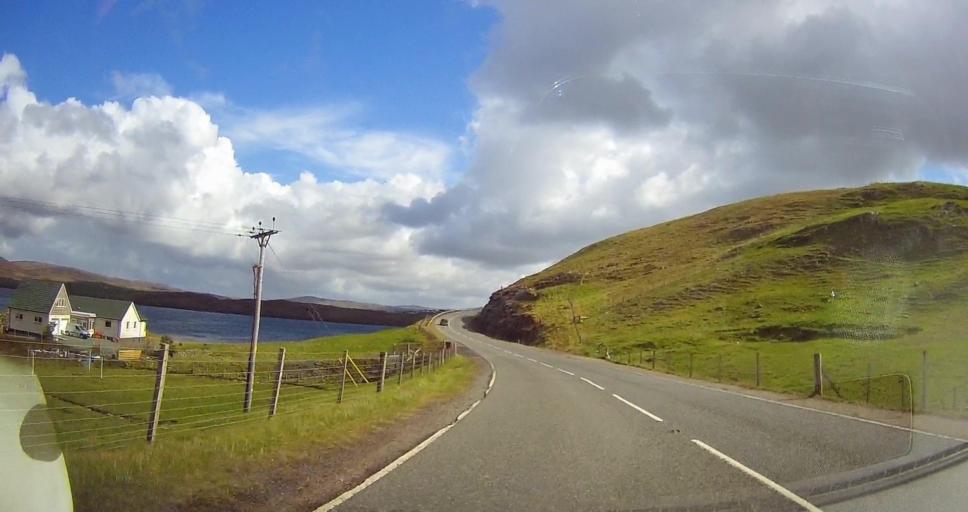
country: GB
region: Scotland
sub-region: Shetland Islands
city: Lerwick
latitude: 60.4042
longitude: -1.3857
